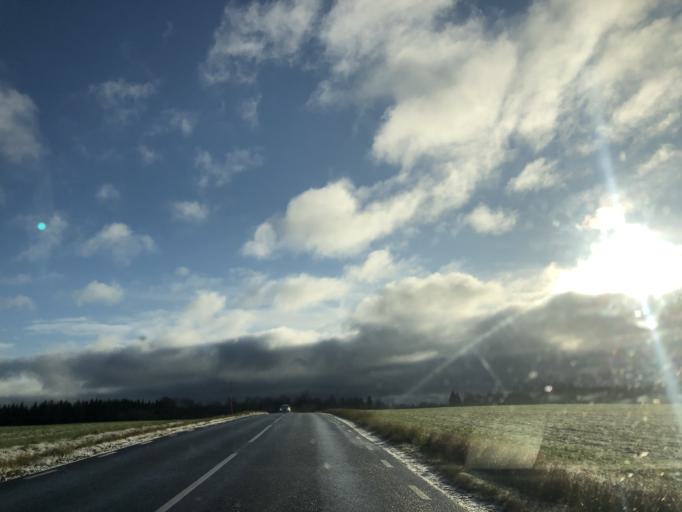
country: SE
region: Vaestra Goetaland
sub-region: Tranemo Kommun
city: Limmared
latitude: 57.6252
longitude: 13.4566
